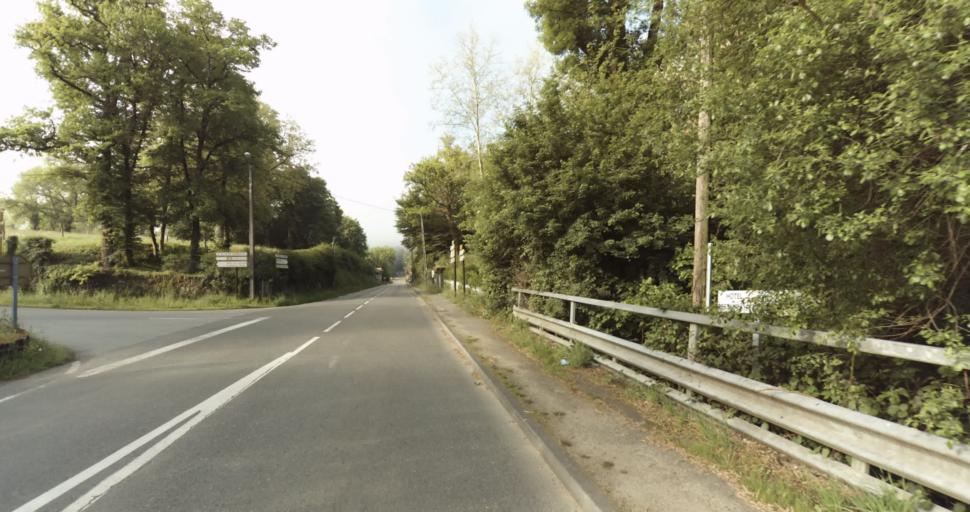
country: FR
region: Limousin
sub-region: Departement de la Haute-Vienne
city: Le Vigen
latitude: 45.7496
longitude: 1.2889
